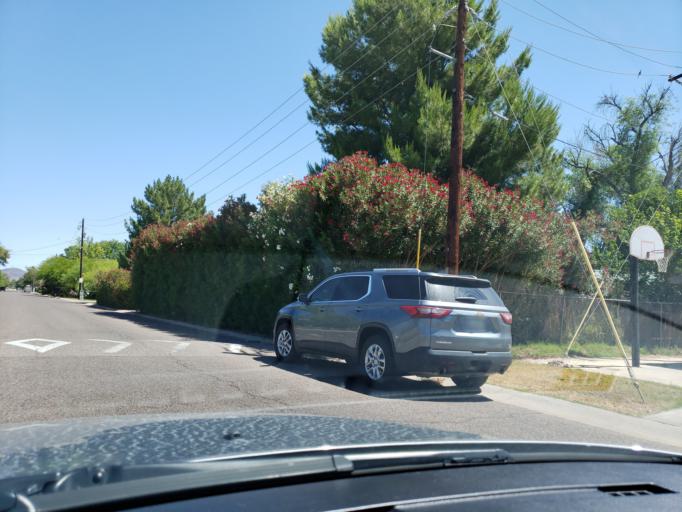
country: US
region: Arizona
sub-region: Maricopa County
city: Phoenix
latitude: 33.5210
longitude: -112.0868
